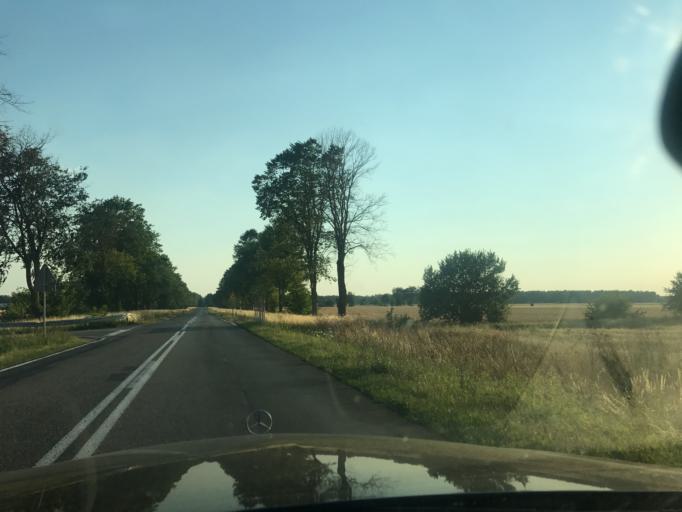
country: PL
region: Lublin Voivodeship
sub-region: Powiat parczewski
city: Jablon
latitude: 51.7107
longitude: 23.0765
